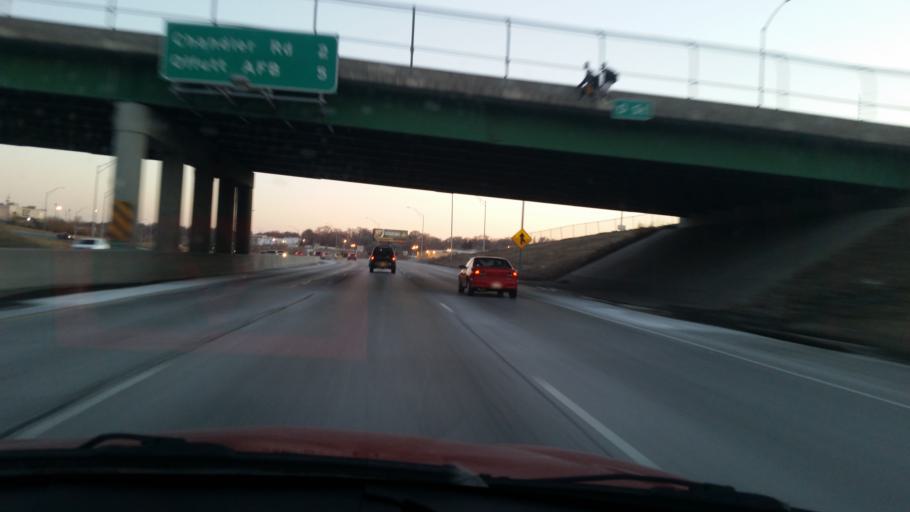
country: US
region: Nebraska
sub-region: Douglas County
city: Omaha
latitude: 41.2060
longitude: -95.9494
